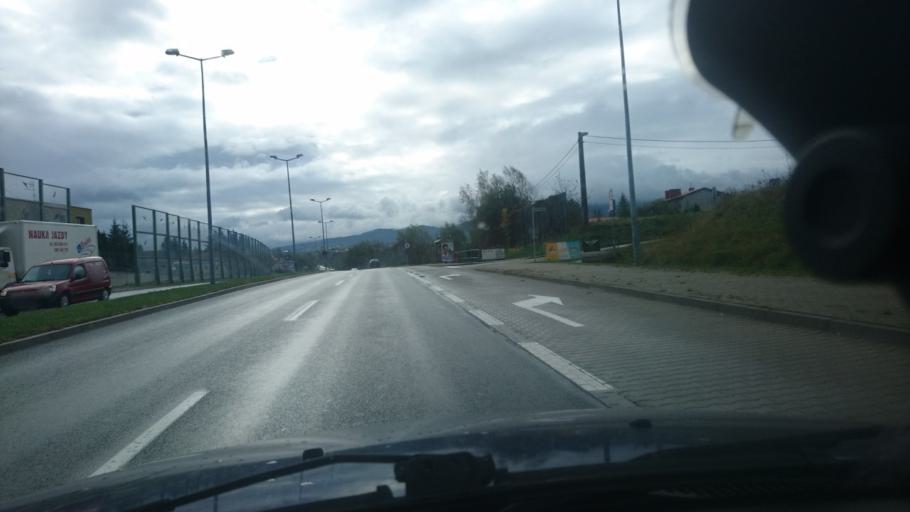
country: PL
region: Silesian Voivodeship
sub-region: Bielsko-Biala
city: Bielsko-Biala
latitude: 49.8291
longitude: 19.0126
